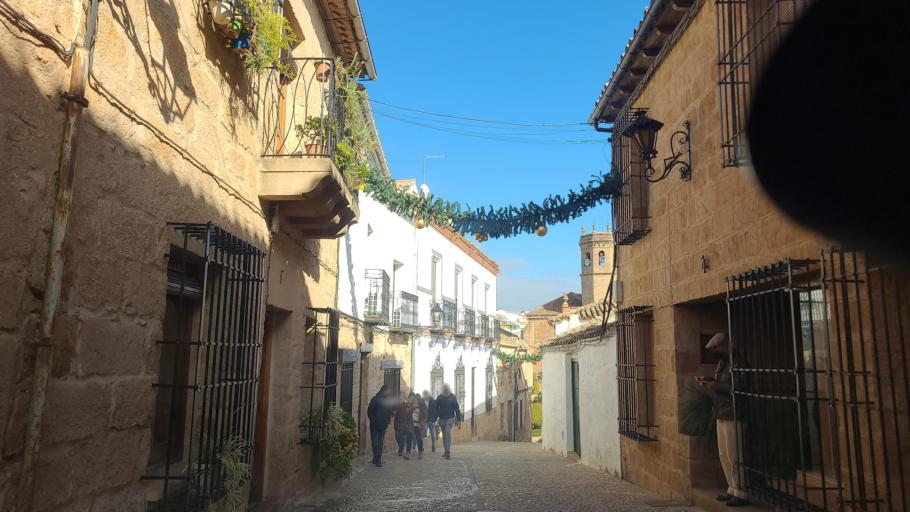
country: ES
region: Andalusia
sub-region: Provincia de Jaen
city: Banos de la Encina
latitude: 38.1703
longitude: -3.7749
